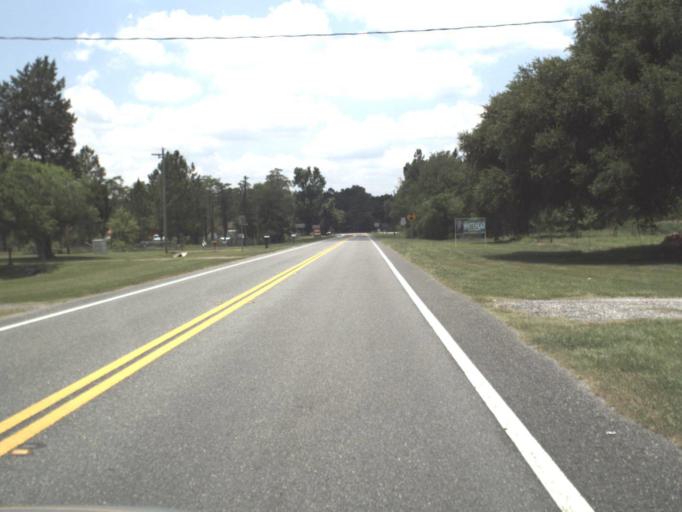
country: US
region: Florida
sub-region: Union County
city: Lake Butler
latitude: 30.0701
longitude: -82.2204
